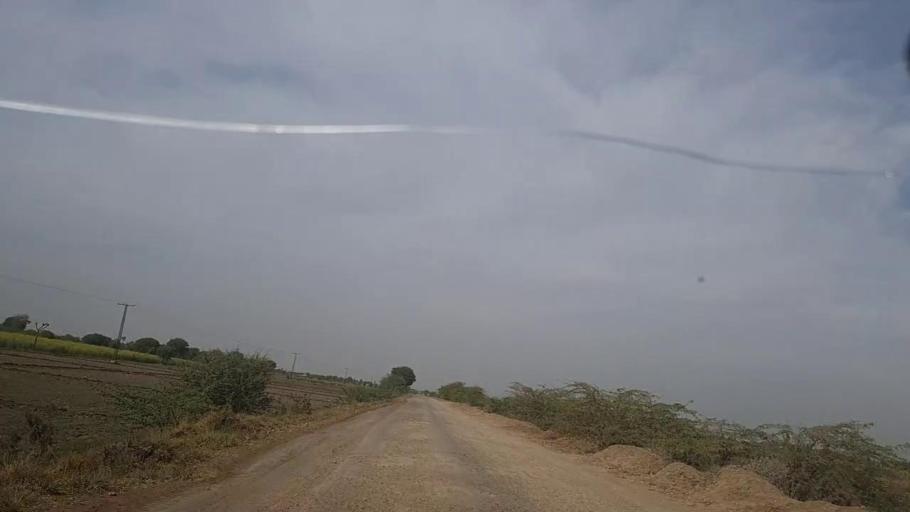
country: PK
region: Sindh
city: Pithoro
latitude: 25.5564
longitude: 69.3628
